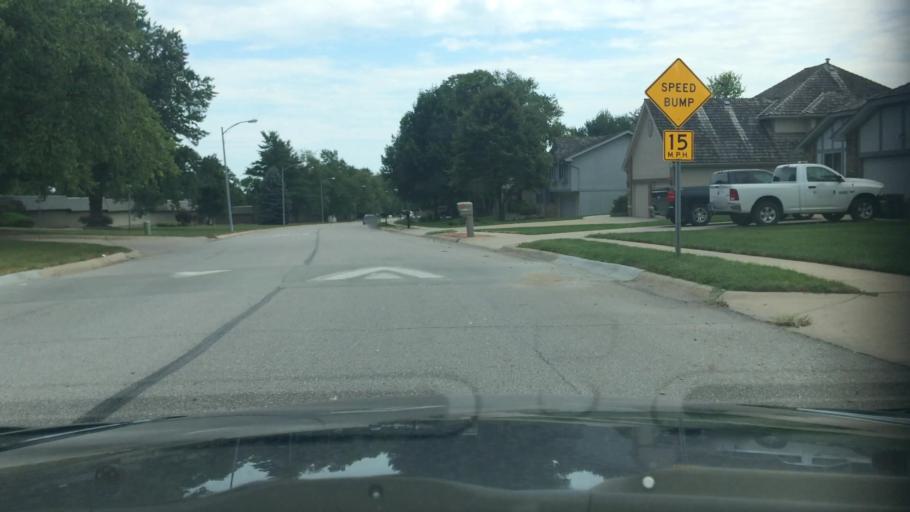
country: US
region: Nebraska
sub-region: Douglas County
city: Ralston
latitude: 41.1951
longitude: -96.0680
